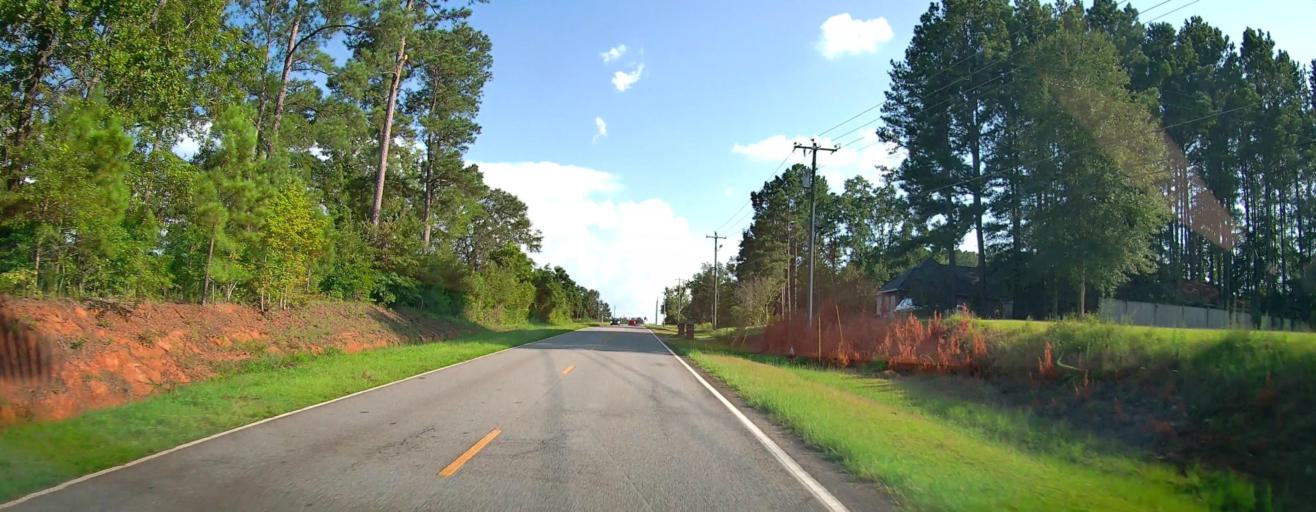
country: US
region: Georgia
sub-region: Houston County
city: Robins Air Force Base
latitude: 32.5547
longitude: -83.6045
